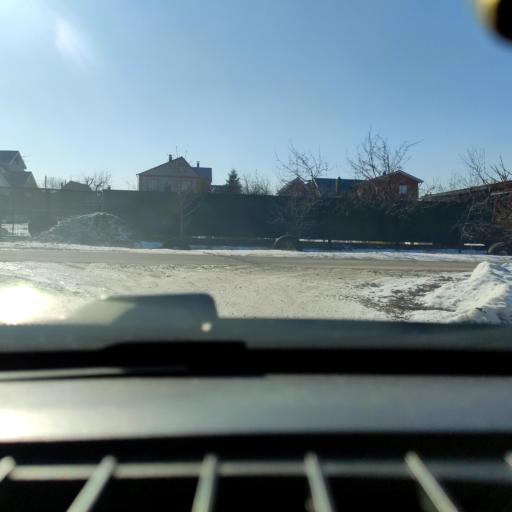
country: RU
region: Voronezj
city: Novaya Usman'
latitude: 51.6639
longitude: 39.3358
